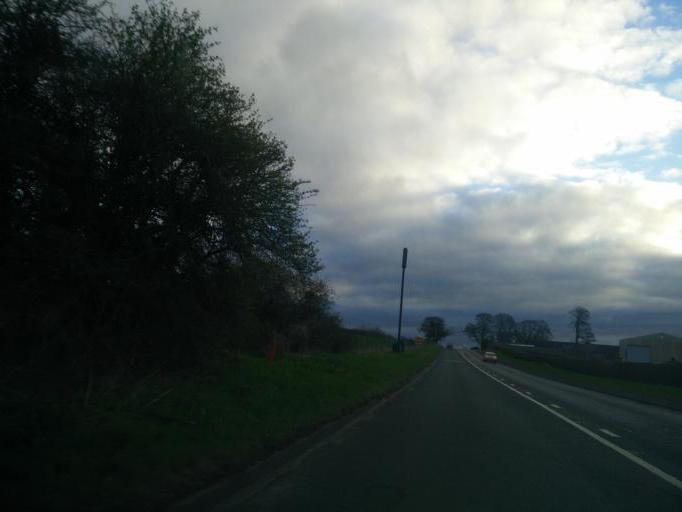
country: GB
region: England
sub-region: County Durham
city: Ushaw Moor
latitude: 54.7444
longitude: -1.6355
